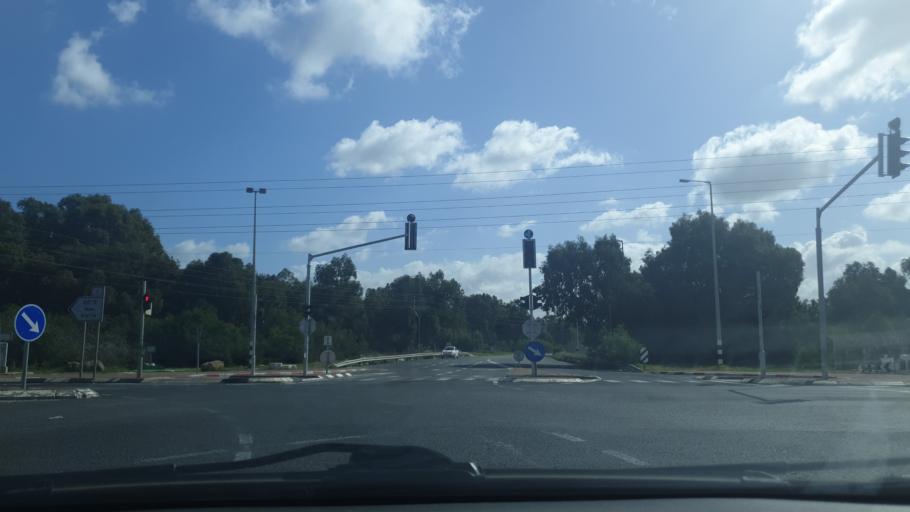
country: IL
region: Haifa
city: Qesarya
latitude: 32.5007
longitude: 34.9279
